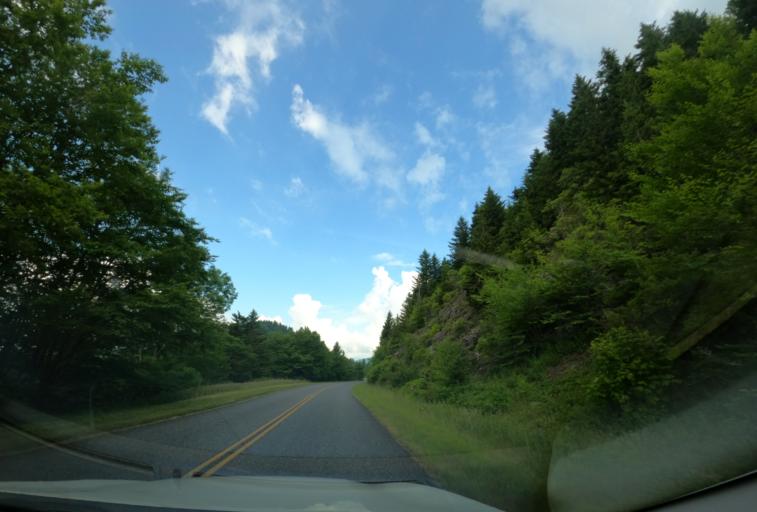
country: US
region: North Carolina
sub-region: Haywood County
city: Hazelwood
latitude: 35.3748
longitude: -83.0037
